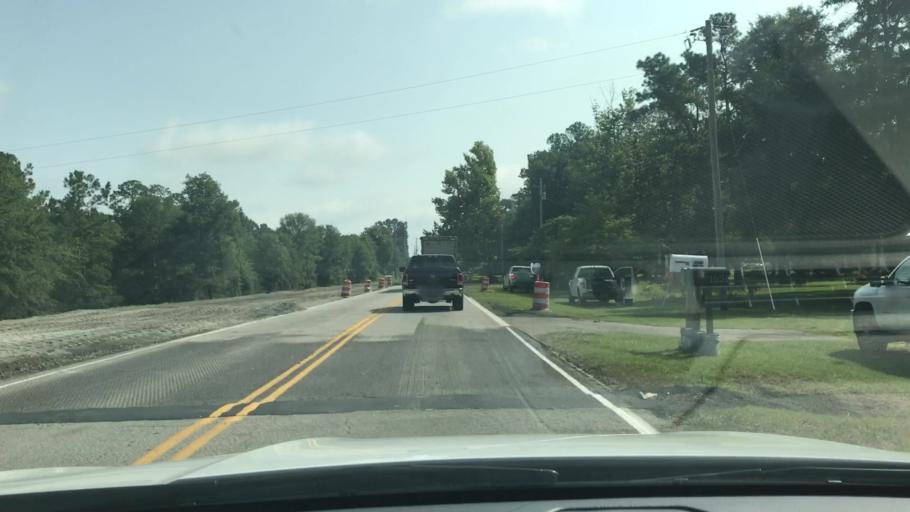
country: US
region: South Carolina
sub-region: Horry County
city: Socastee
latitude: 33.6699
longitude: -79.1411
